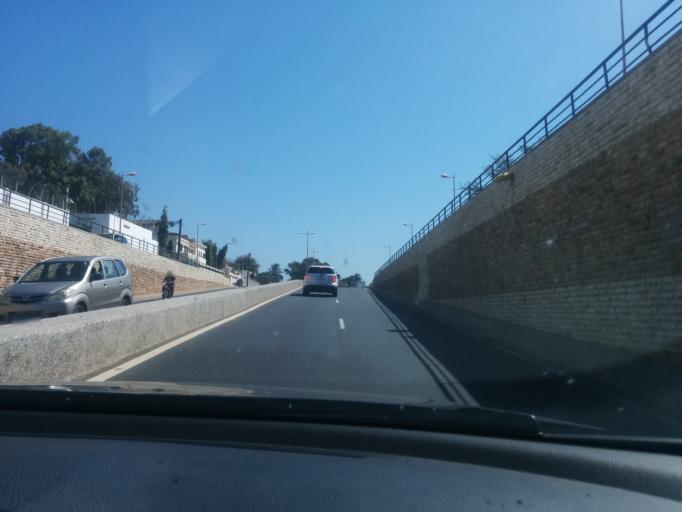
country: SN
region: Dakar
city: Mermoz Boabab
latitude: 14.7009
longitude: -17.4750
